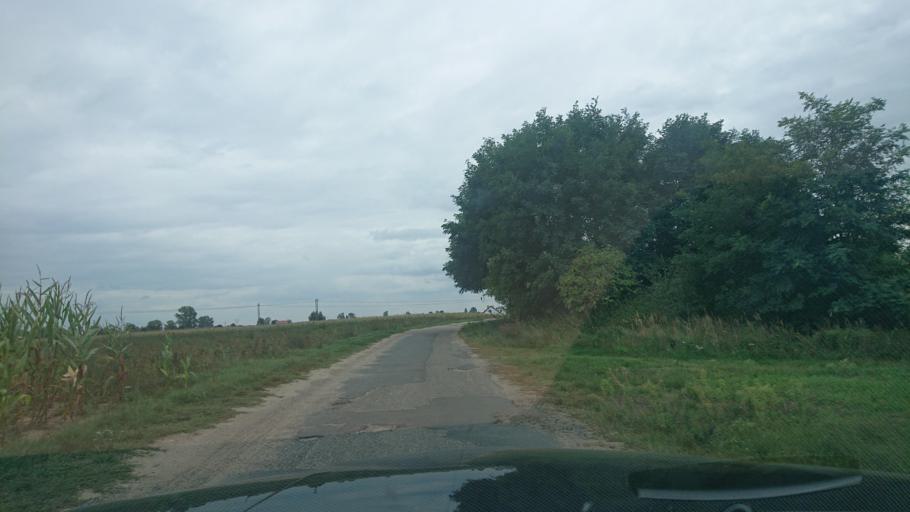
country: PL
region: Greater Poland Voivodeship
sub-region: Powiat gnieznienski
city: Niechanowo
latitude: 52.4783
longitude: 17.6198
